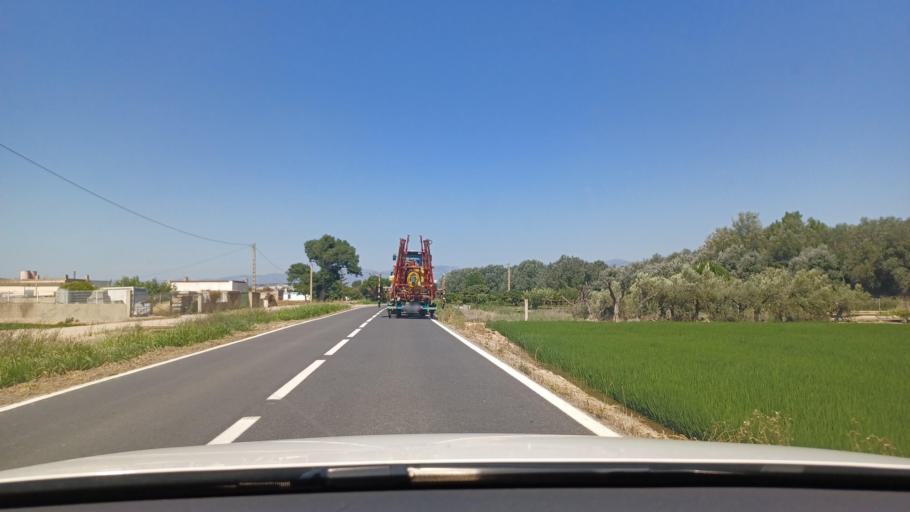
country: ES
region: Catalonia
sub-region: Provincia de Tarragona
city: Amposta
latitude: 40.7043
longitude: 0.6057
